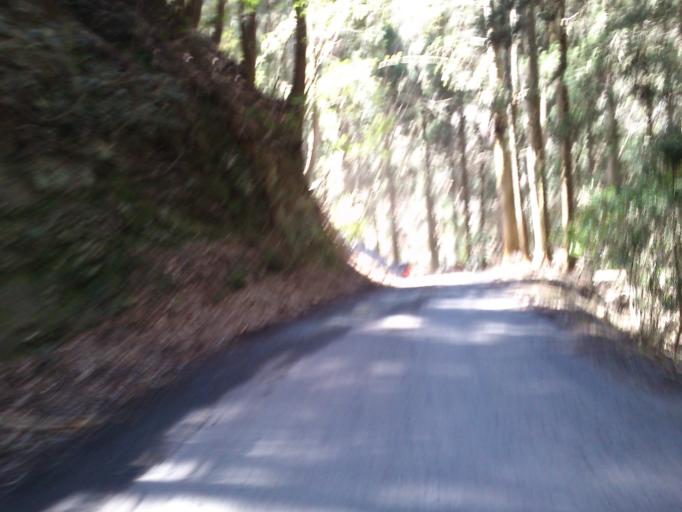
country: JP
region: Shiga Prefecture
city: Otsu-shi
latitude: 34.9490
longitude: 135.8454
